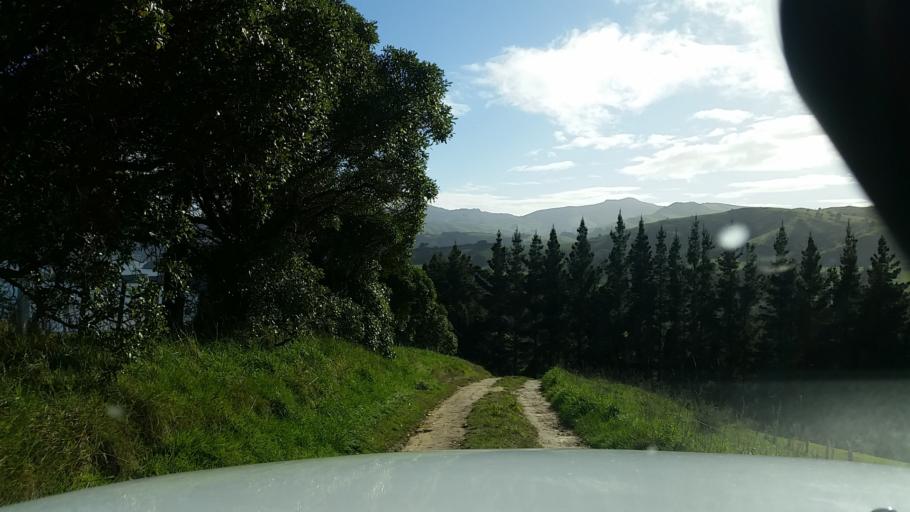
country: NZ
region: Canterbury
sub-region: Christchurch City
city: Christchurch
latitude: -43.7896
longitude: 172.9690
